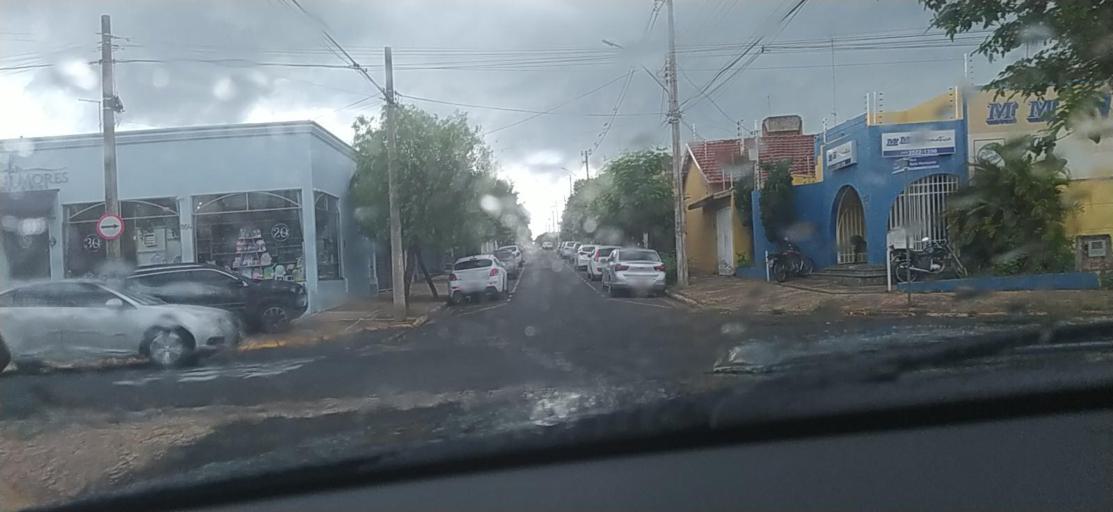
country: BR
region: Sao Paulo
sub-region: Catanduva
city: Catanduva
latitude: -21.1391
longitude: -48.9776
